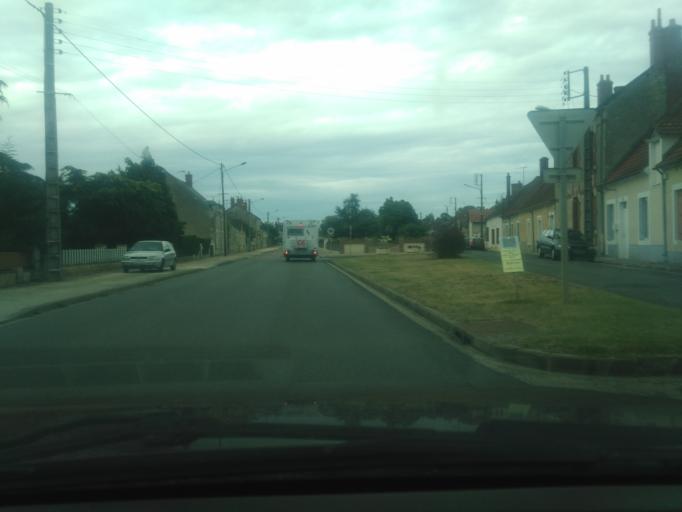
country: FR
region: Centre
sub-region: Departement du Cher
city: Sancoins
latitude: 46.8240
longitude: 2.9161
